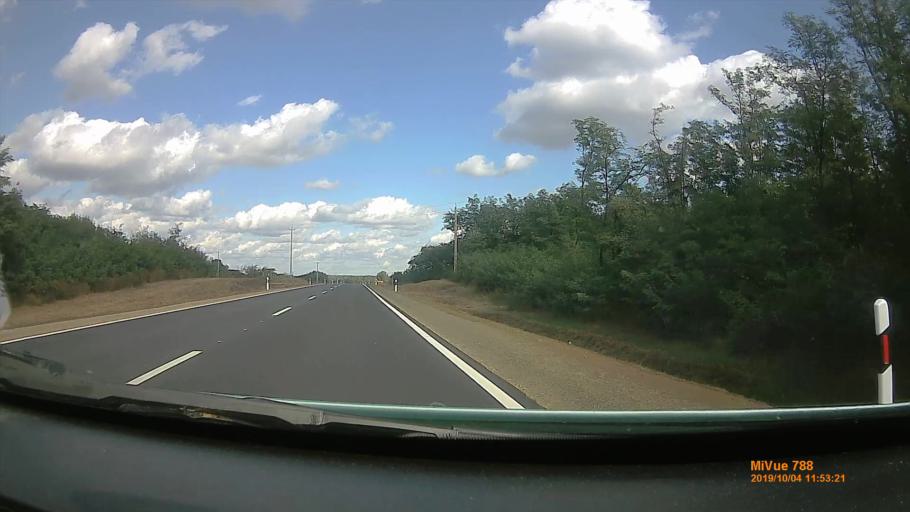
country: HU
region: Szabolcs-Szatmar-Bereg
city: Nyirtelek
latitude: 48.0086
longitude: 21.6757
